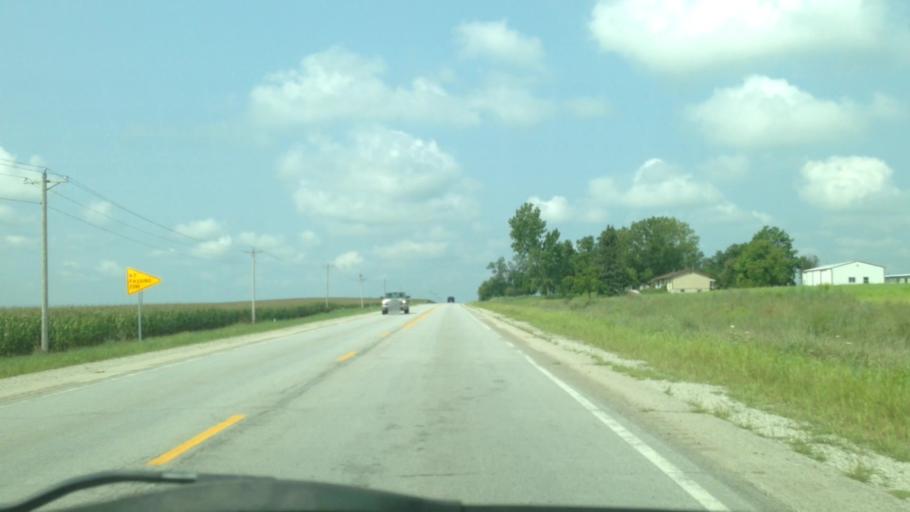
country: US
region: Iowa
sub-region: Benton County
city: Walford
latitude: 41.8763
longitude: -91.8478
